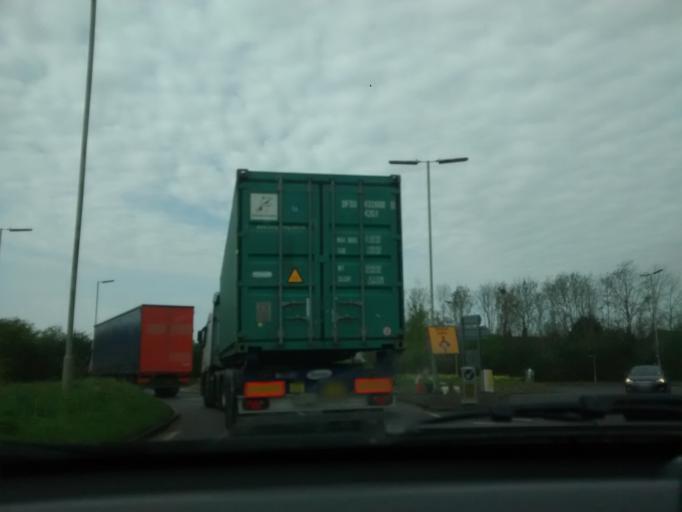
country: GB
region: England
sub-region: Oxfordshire
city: Bicester
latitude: 51.8875
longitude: -1.1374
